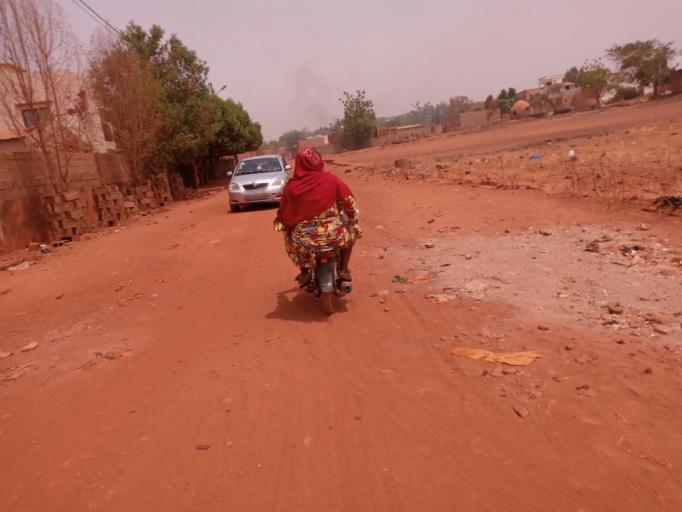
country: ML
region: Bamako
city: Bamako
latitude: 12.6742
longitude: -7.9099
